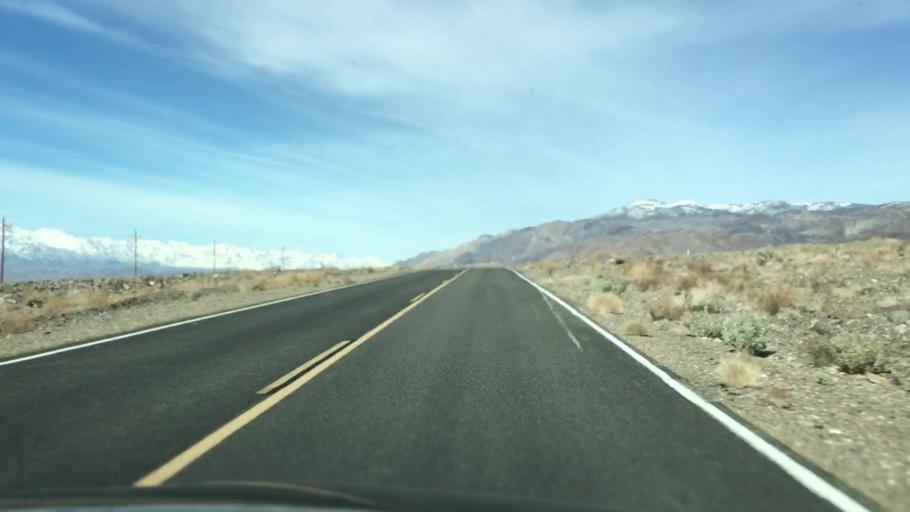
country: US
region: California
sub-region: Inyo County
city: Lone Pine
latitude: 36.4626
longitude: -117.8472
